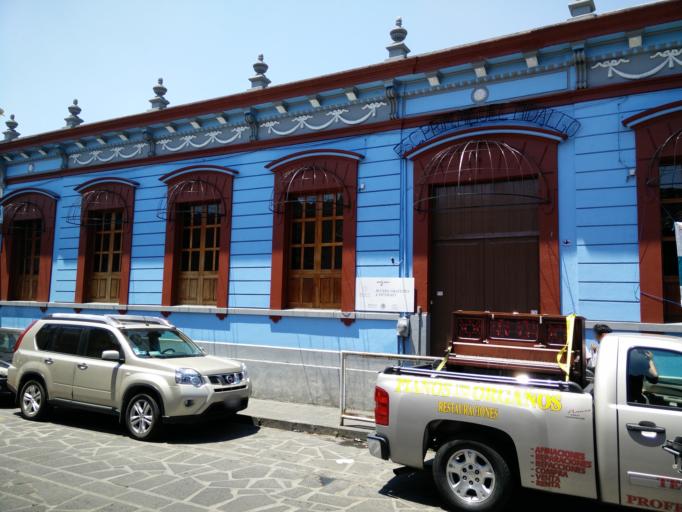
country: MX
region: Veracruz
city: Coatepec
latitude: 19.4530
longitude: -96.9577
